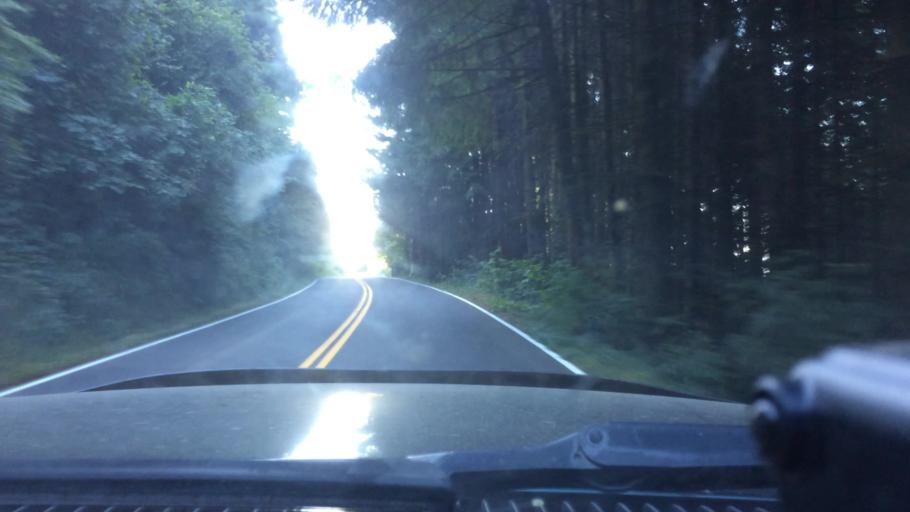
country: US
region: Oregon
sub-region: Yamhill County
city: Newberg
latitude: 45.3439
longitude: -122.9583
